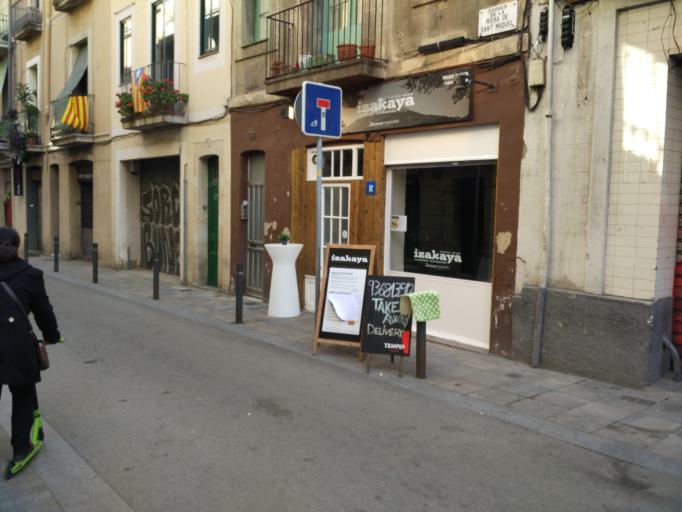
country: ES
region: Catalonia
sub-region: Provincia de Barcelona
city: Gracia
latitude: 41.3987
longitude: 2.1546
